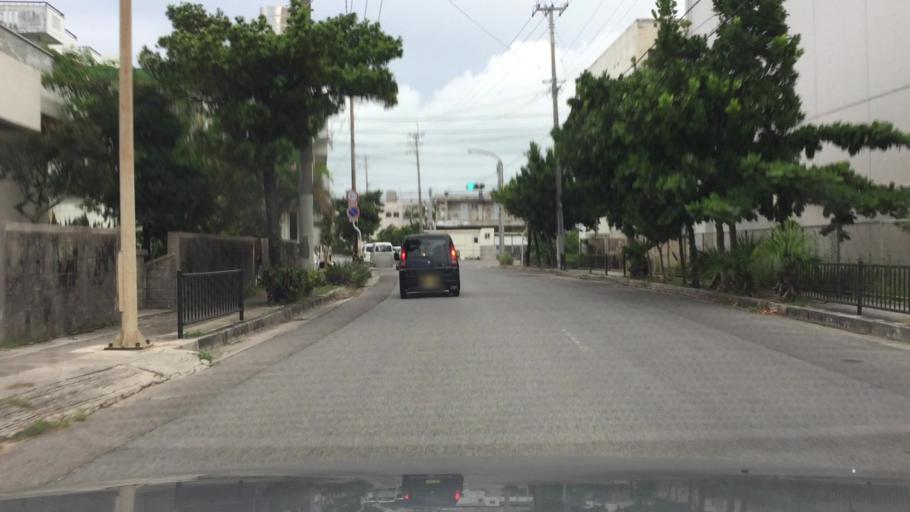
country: JP
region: Okinawa
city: Ishigaki
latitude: 24.3489
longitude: 124.1583
